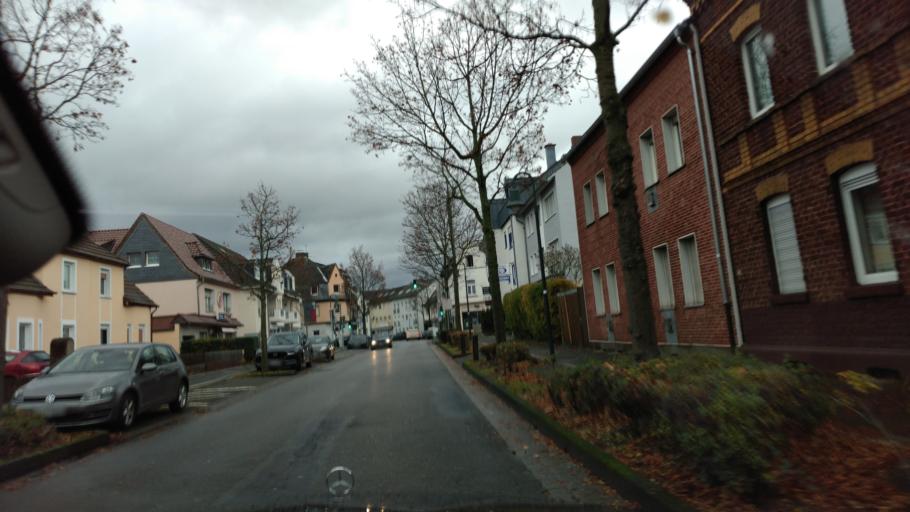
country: DE
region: North Rhine-Westphalia
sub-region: Regierungsbezirk Koln
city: Troisdorf
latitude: 50.8101
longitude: 7.1395
